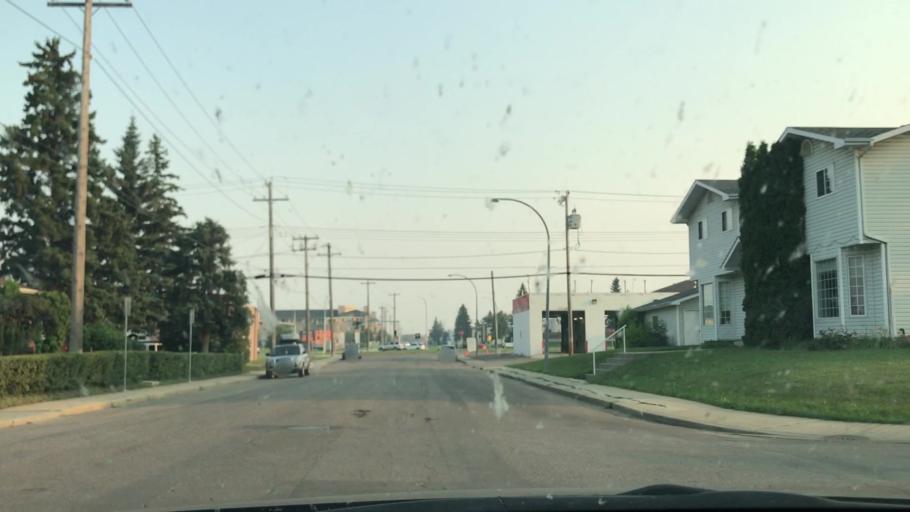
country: CA
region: Alberta
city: Edmonton
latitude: 53.5191
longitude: -113.4368
